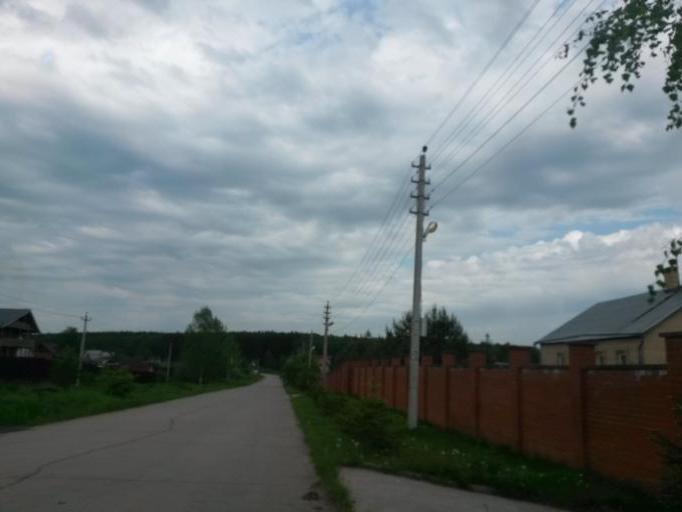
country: RU
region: Moskovskaya
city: Melikhovo
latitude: 55.1549
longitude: 37.6309
